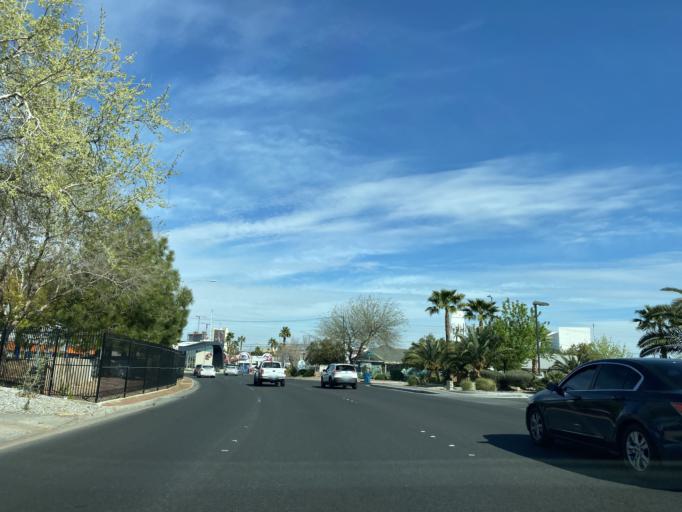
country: US
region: Nevada
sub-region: Clark County
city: Las Vegas
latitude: 36.1566
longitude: -115.1365
